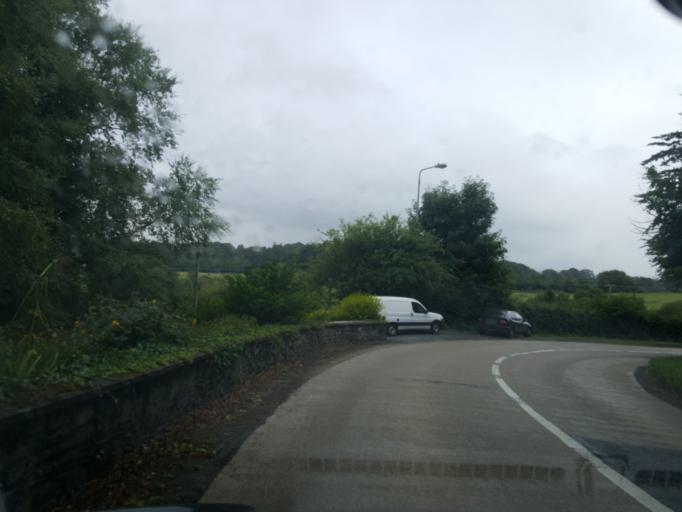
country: IE
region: Leinster
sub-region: Kildare
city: Kilcullen
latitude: 53.1293
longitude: -6.7424
